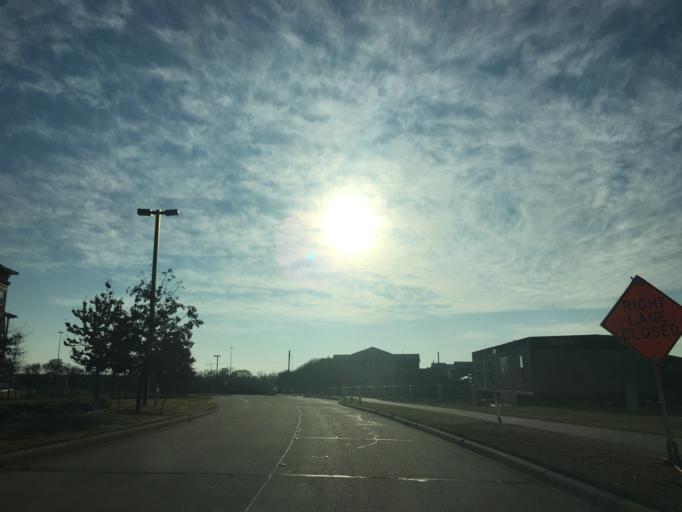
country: US
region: Texas
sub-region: Denton County
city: The Colony
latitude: 33.0895
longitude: -96.8427
